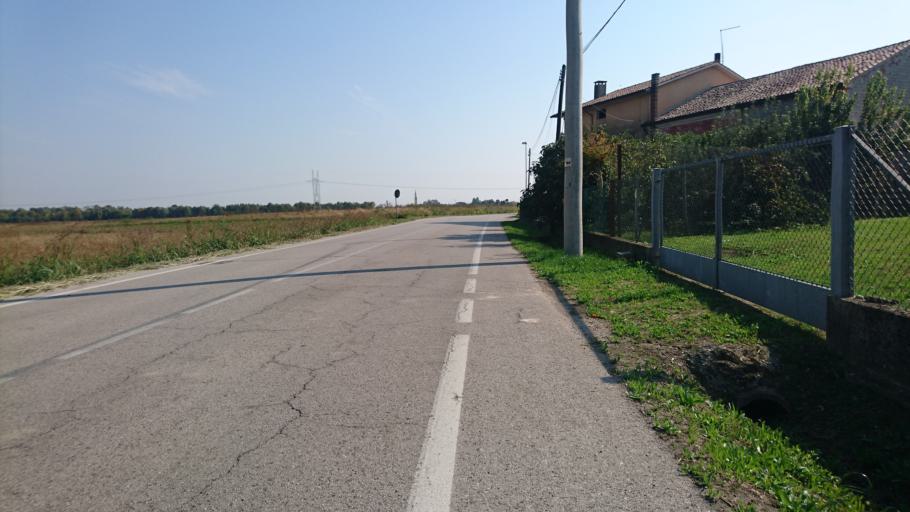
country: IT
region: Veneto
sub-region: Provincia di Vicenza
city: Grumolo delle Abbadesse
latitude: 45.5413
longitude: 11.6719
